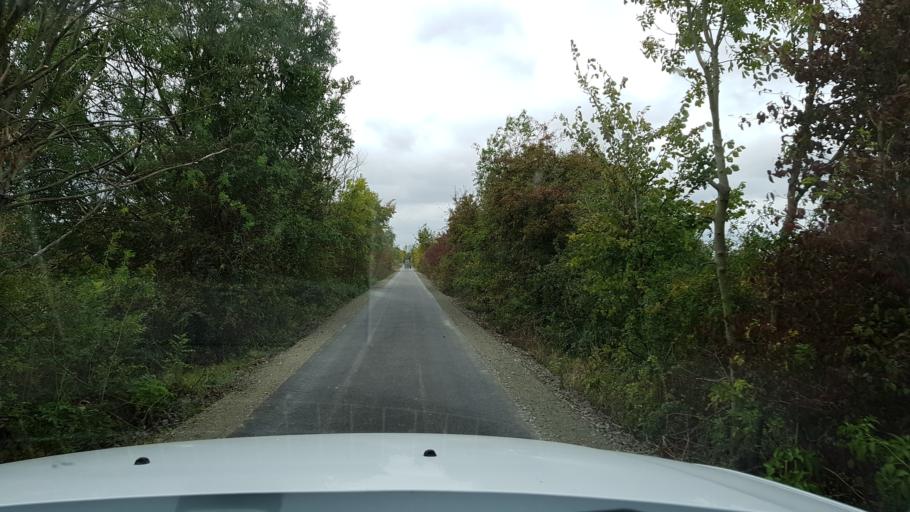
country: PL
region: West Pomeranian Voivodeship
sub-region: Powiat gryfinski
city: Moryn
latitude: 52.8658
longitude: 14.3347
